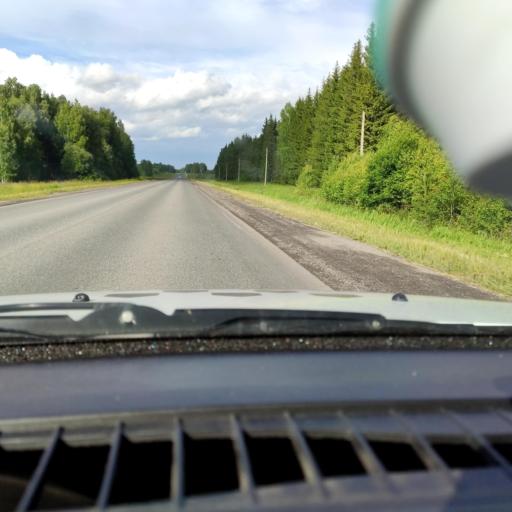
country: RU
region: Perm
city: Orda
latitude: 57.2387
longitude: 56.9817
